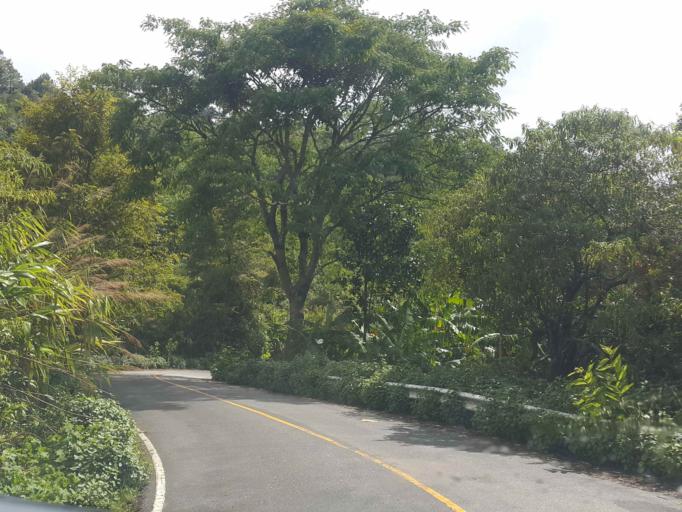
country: TH
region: Chiang Mai
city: Mae Chaem
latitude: 18.5142
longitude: 98.5232
